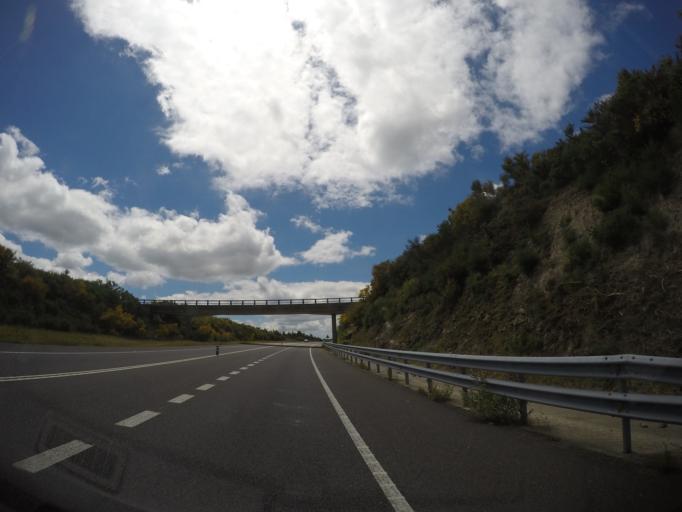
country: ES
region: Aragon
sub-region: Provincia de Zaragoza
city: Fuentes de Ebro
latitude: 41.4973
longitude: -0.6435
